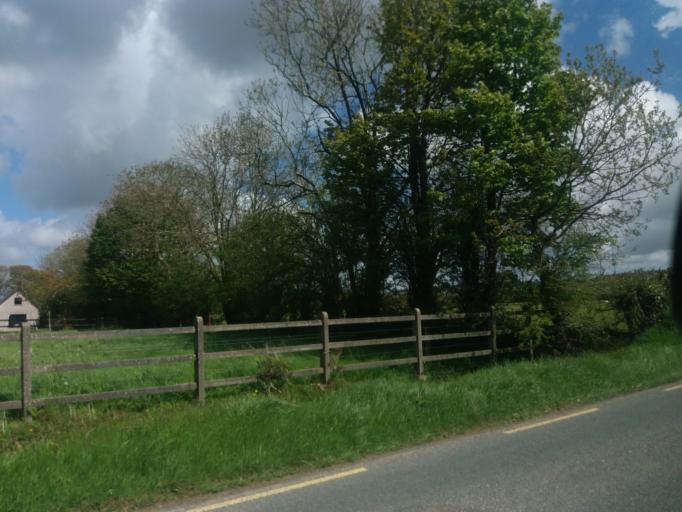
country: IE
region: Leinster
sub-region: Loch Garman
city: Loch Garman
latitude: 52.2887
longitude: -6.6120
